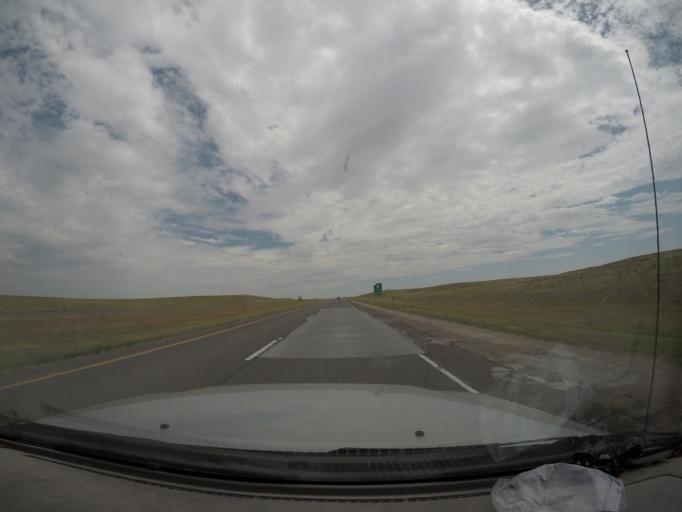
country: US
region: Wyoming
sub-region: Laramie County
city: Pine Bluffs
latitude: 41.1917
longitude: -103.9175
